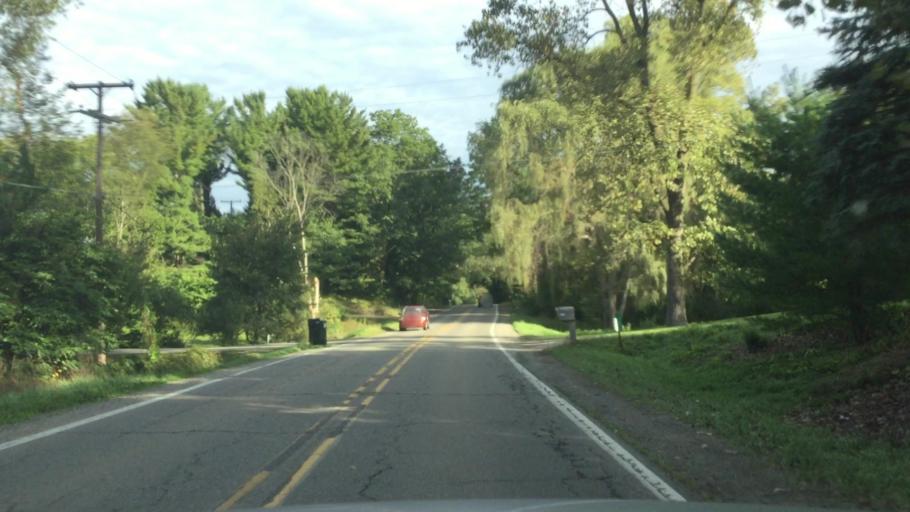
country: US
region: Michigan
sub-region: Livingston County
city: Brighton
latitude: 42.4860
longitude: -83.8518
